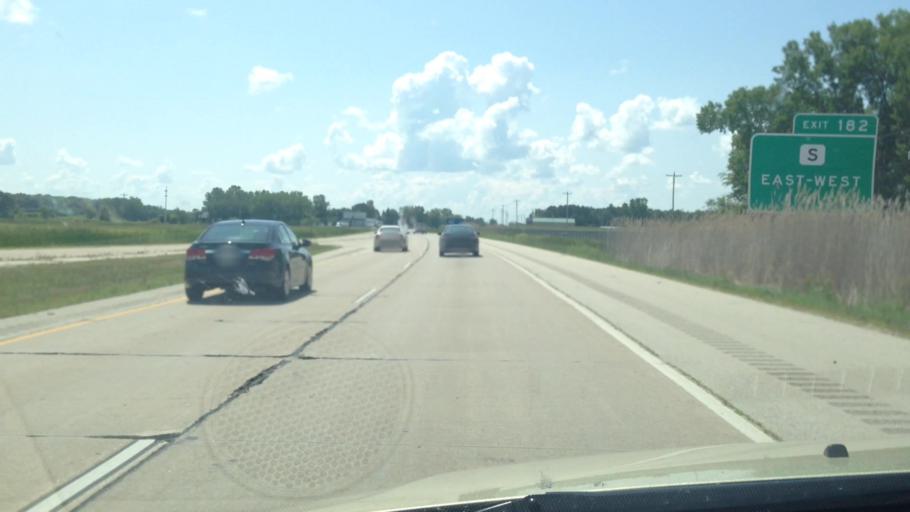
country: US
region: Wisconsin
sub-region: Brown County
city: Suamico
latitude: 44.7408
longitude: -88.0521
